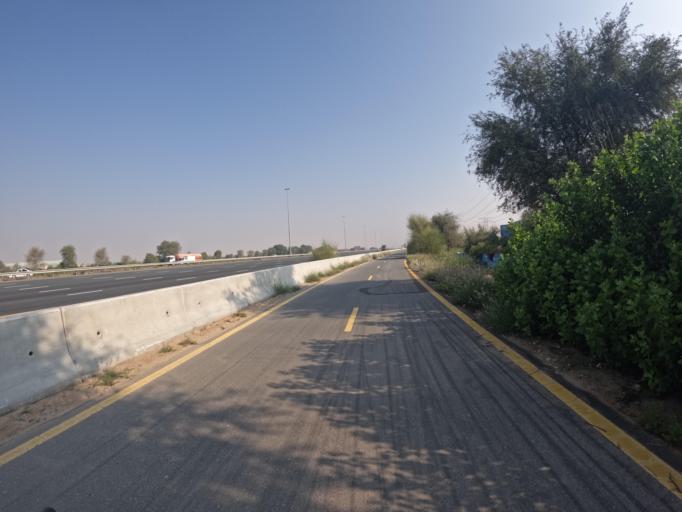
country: AE
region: Dubai
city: Dubai
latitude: 25.0422
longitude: 55.3035
